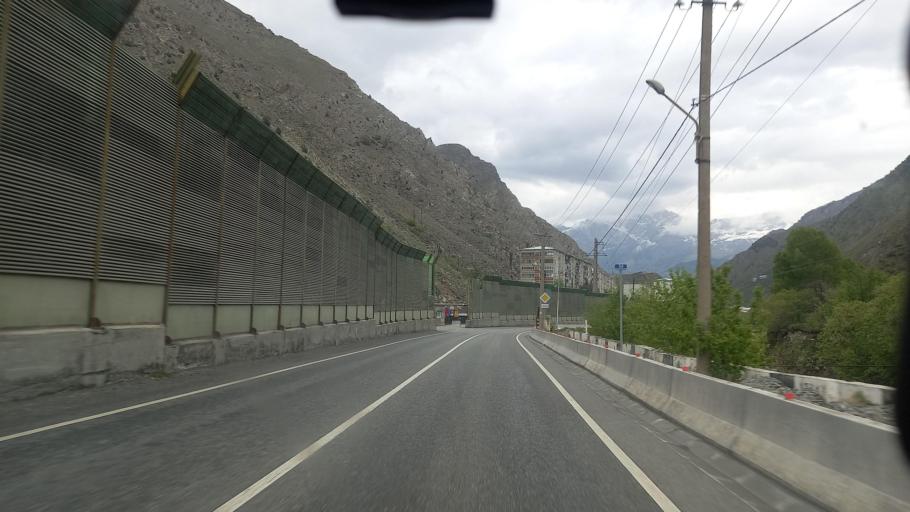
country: RU
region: North Ossetia
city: Mizur
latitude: 42.8515
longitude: 44.0620
